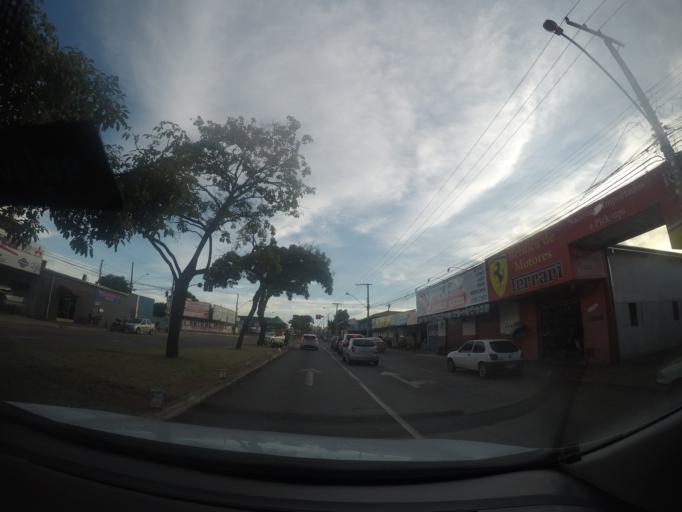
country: BR
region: Goias
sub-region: Goiania
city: Goiania
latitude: -16.6805
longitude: -49.3194
